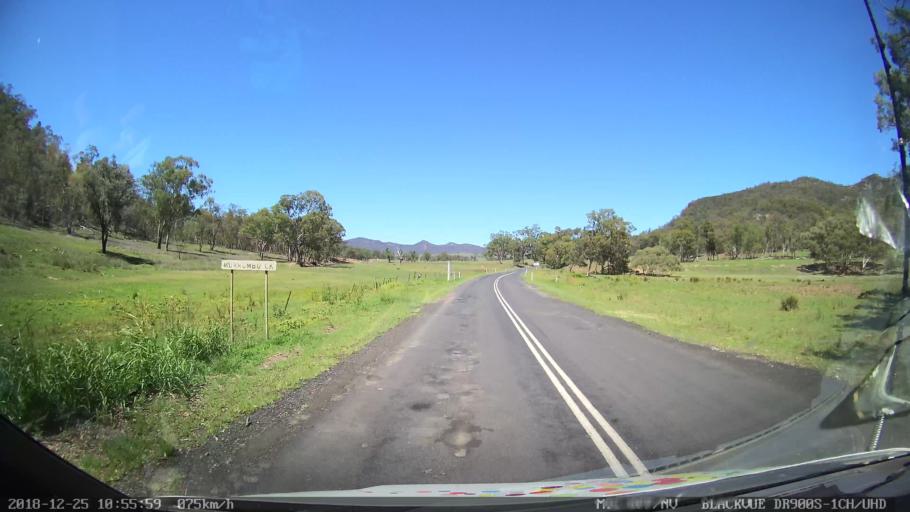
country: AU
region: New South Wales
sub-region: Upper Hunter Shire
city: Merriwa
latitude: -32.3991
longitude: 150.2677
